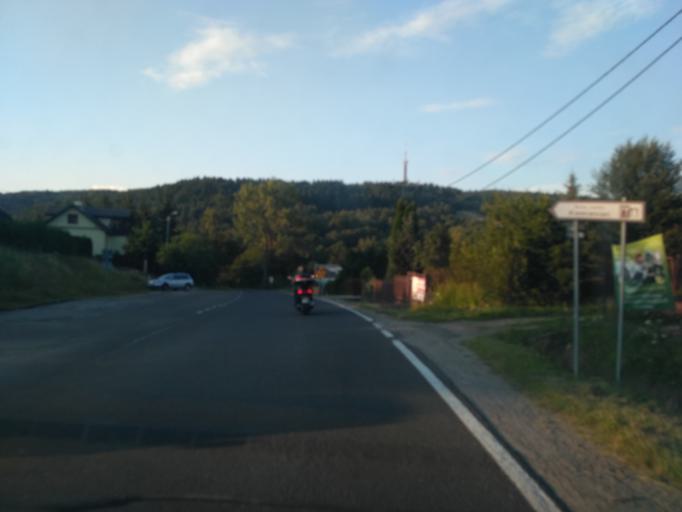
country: PL
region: Subcarpathian Voivodeship
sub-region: Powiat krosnienski
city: Korczyna
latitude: 49.7456
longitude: 21.8028
